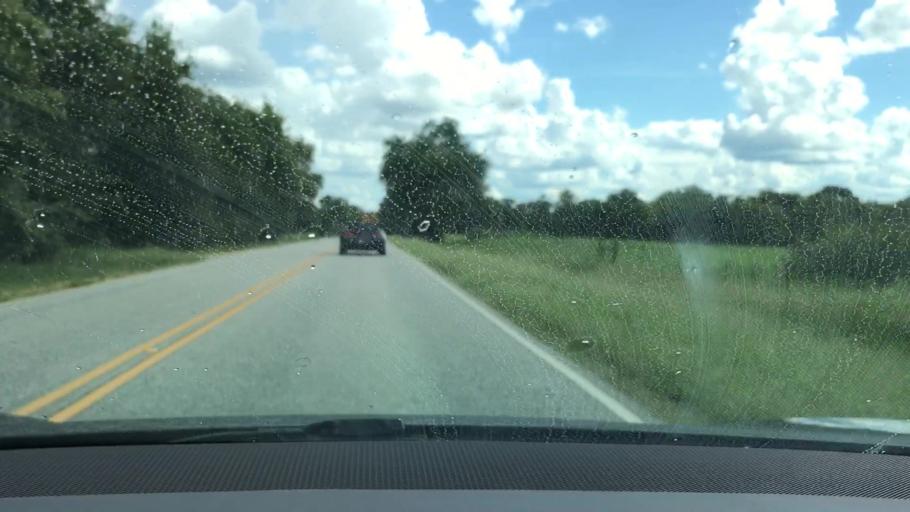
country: US
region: Alabama
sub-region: Montgomery County
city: Pike Road
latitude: 32.2398
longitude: -86.0932
